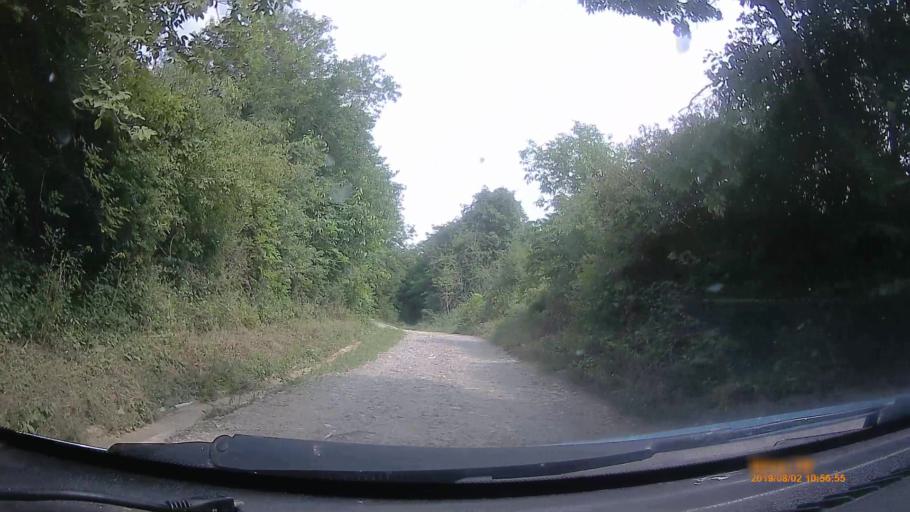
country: HU
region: Baranya
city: Buekkoesd
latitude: 46.0980
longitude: 17.9515
